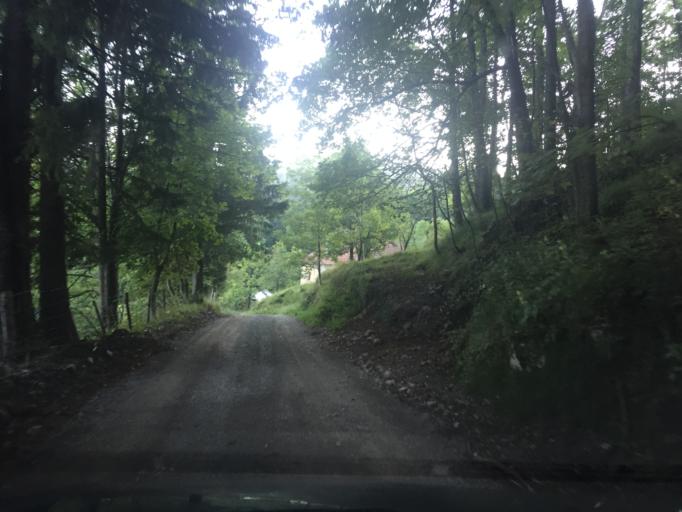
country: SI
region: Ravne na Koroskem
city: Kotlje
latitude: 46.4737
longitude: 14.9741
